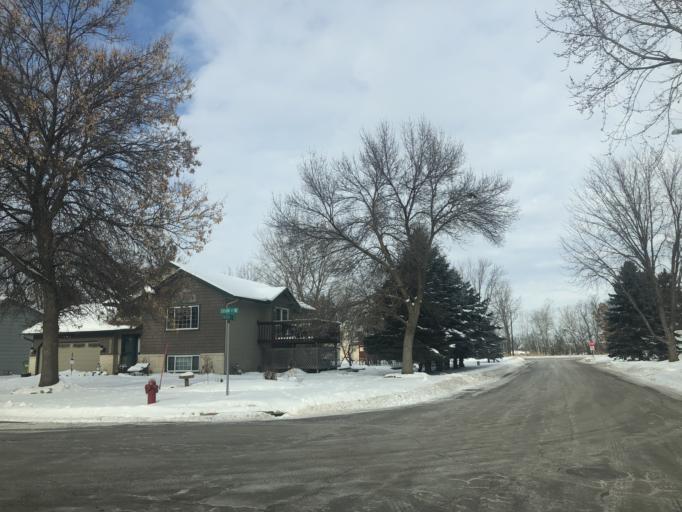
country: US
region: Minnesota
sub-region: Anoka County
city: Circle Pines
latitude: 45.1557
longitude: -93.1613
